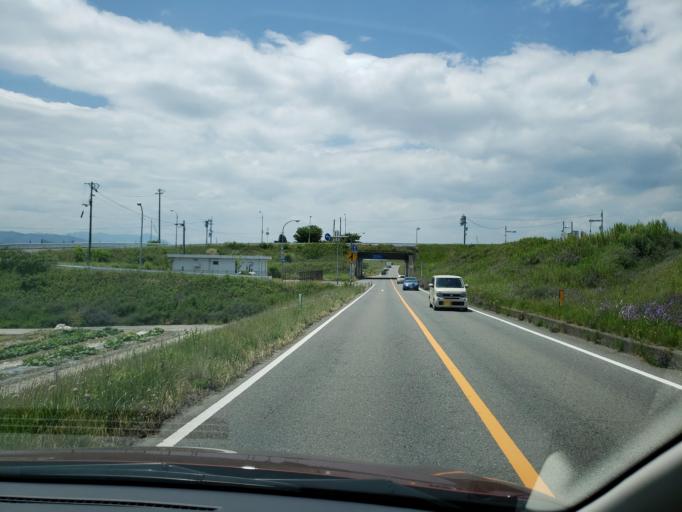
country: JP
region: Tokushima
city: Ishii
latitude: 34.1012
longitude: 134.4393
